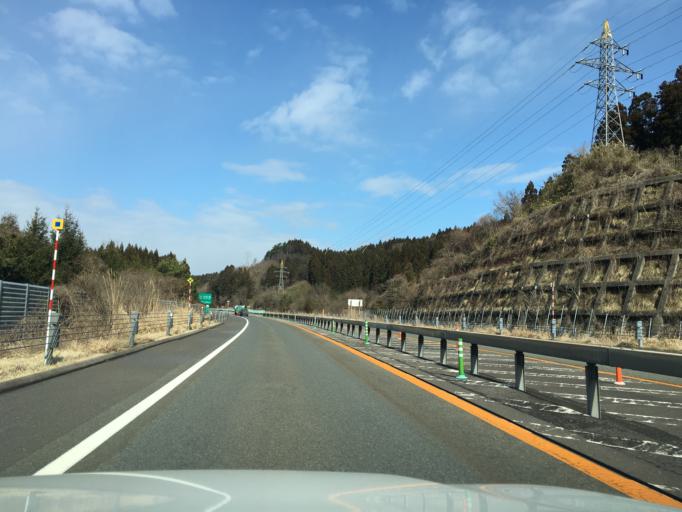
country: JP
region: Akita
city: Akita
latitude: 39.7751
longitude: 140.1195
